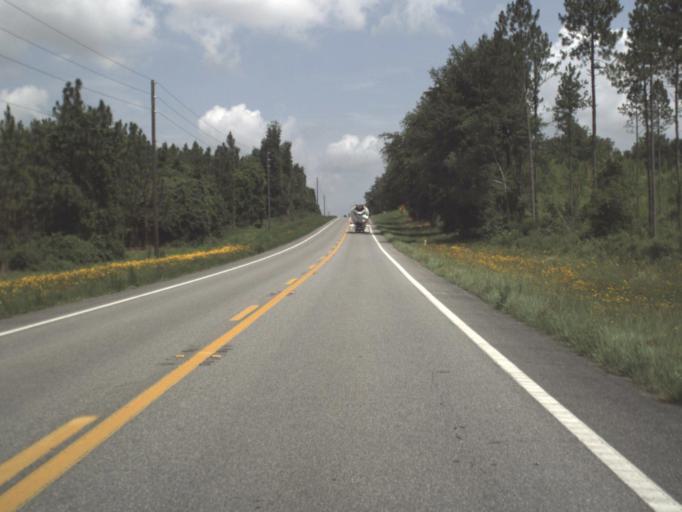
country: US
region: Florida
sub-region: Madison County
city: Madison
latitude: 30.4526
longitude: -83.3494
